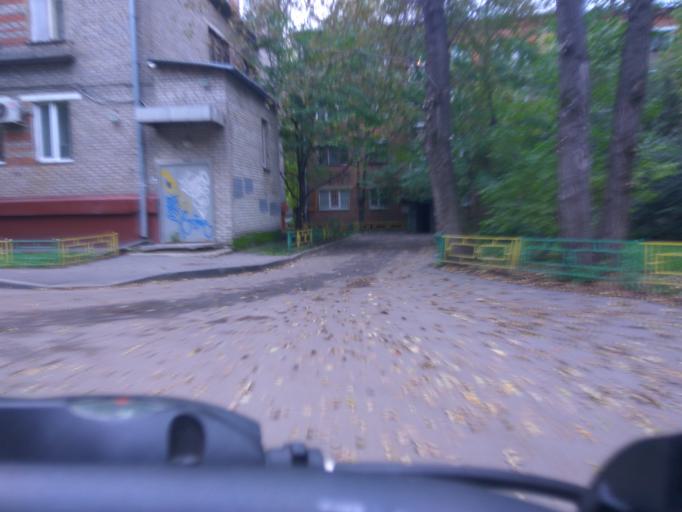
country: RU
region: Moscow
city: Altuf'yevskiy
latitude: 55.8806
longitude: 37.5776
